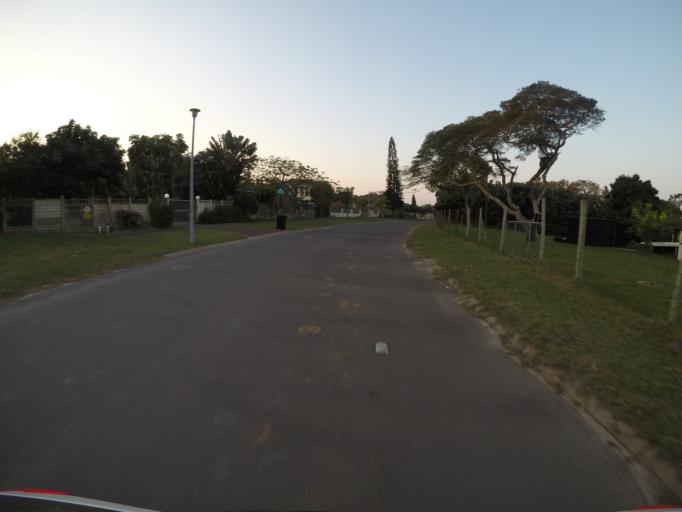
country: ZA
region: KwaZulu-Natal
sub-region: uThungulu District Municipality
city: Richards Bay
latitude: -28.7700
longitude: 32.1214
